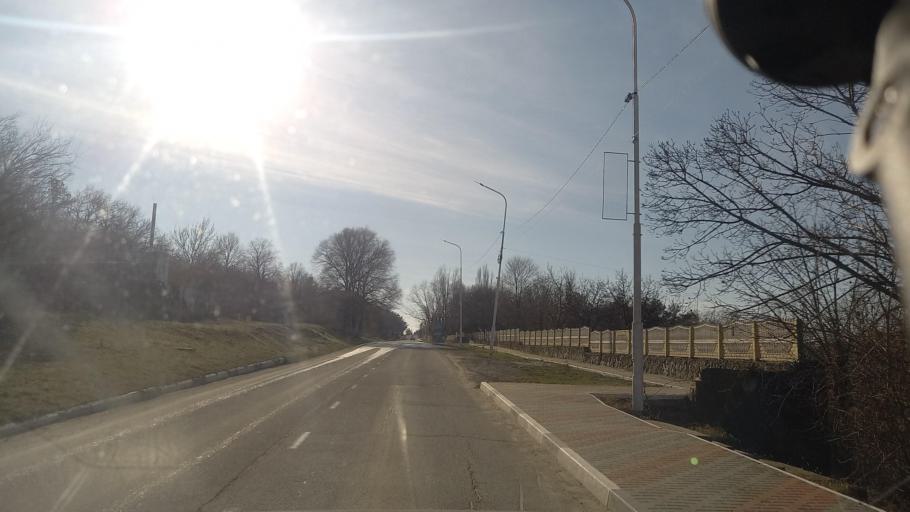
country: RU
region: Krasnodarskiy
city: Kabardinka
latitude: 44.6362
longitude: 37.9167
